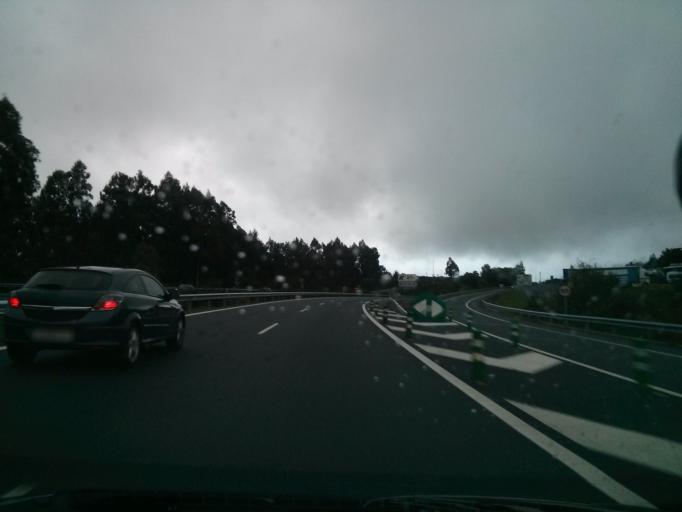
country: ES
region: Galicia
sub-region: Provincia de Ourense
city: Melon
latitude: 42.2087
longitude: -8.2652
